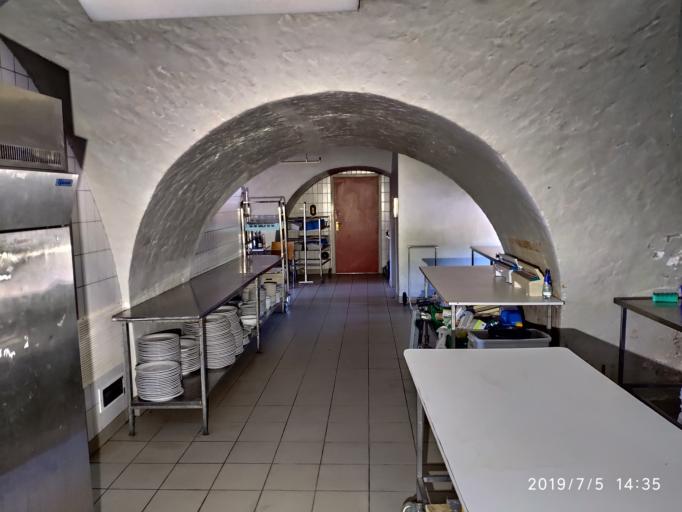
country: NO
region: Akershus
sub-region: Frogn
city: Drobak
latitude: 59.6518
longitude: 10.6096
